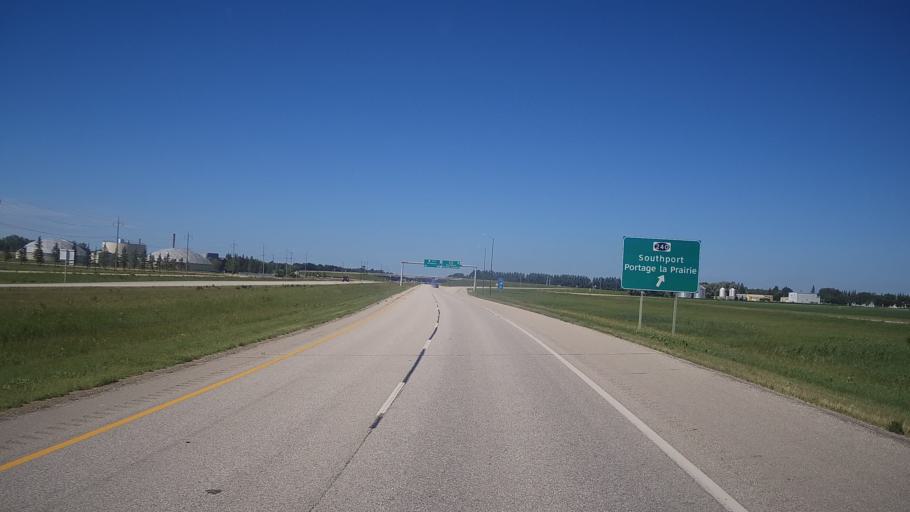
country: CA
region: Manitoba
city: Portage la Prairie
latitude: 49.9581
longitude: -98.2643
